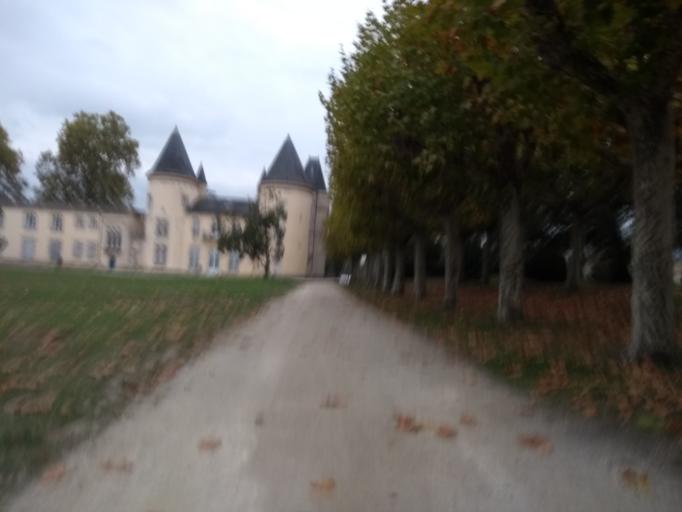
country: FR
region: Aquitaine
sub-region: Departement de la Gironde
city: Talence
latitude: 44.7895
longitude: -0.5921
